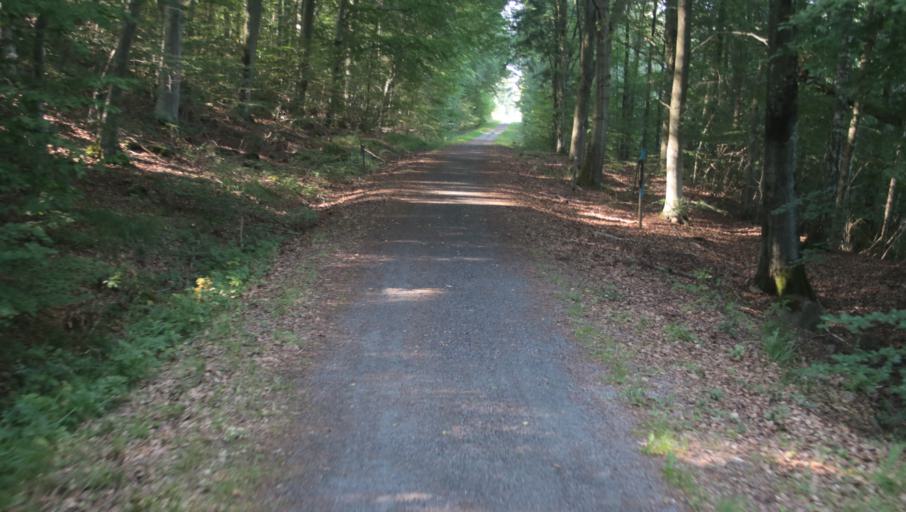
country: SE
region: Blekinge
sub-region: Karlshamns Kommun
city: Svangsta
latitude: 56.2682
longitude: 14.7638
